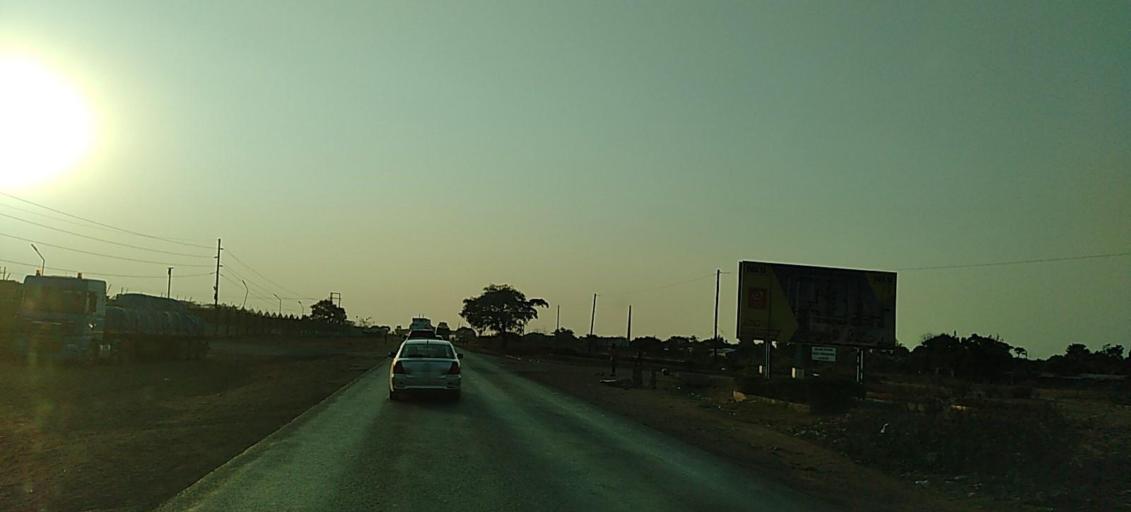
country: ZM
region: Copperbelt
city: Ndola
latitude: -13.0297
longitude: 28.6830
